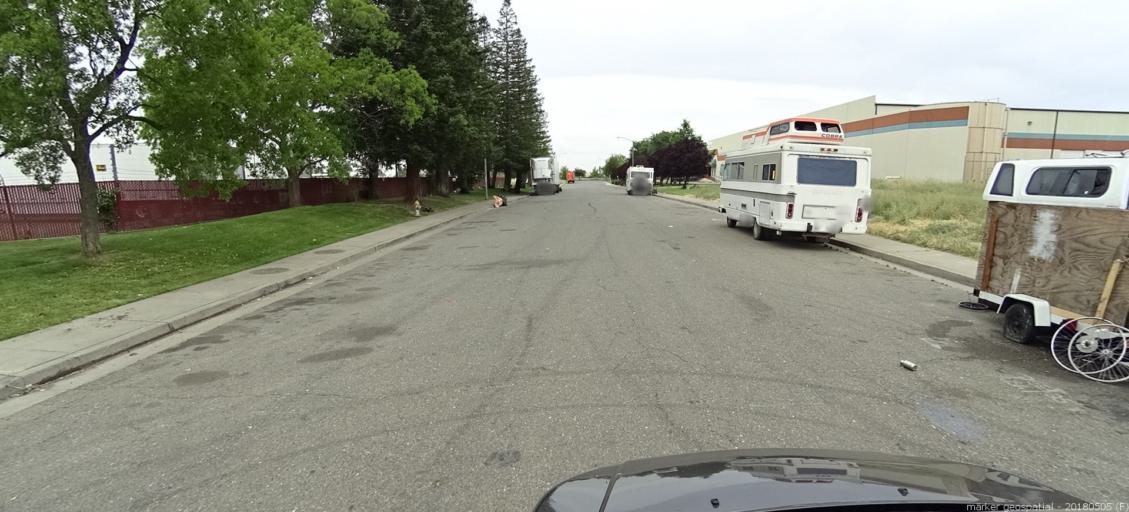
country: US
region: California
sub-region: Sacramento County
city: Rio Linda
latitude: 38.6491
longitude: -121.4257
